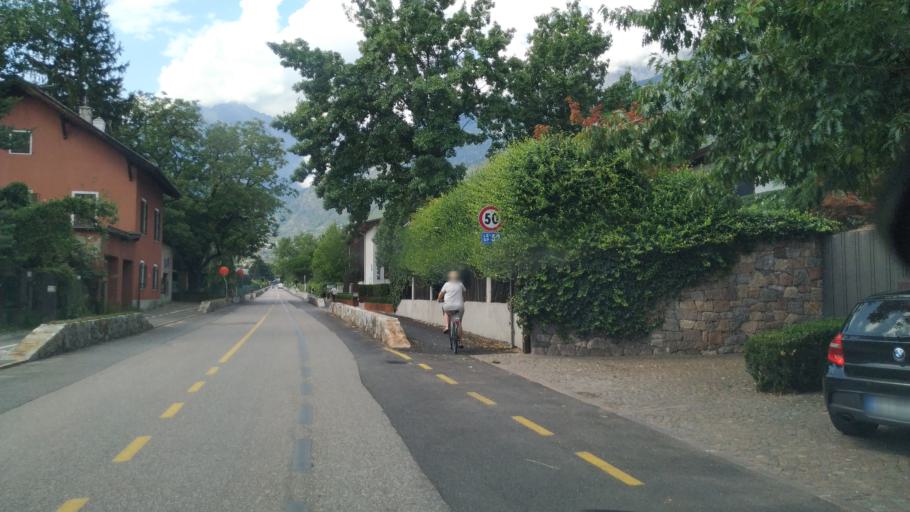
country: IT
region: Trentino-Alto Adige
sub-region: Bolzano
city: Tirolo
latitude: 46.6782
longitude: 11.1440
